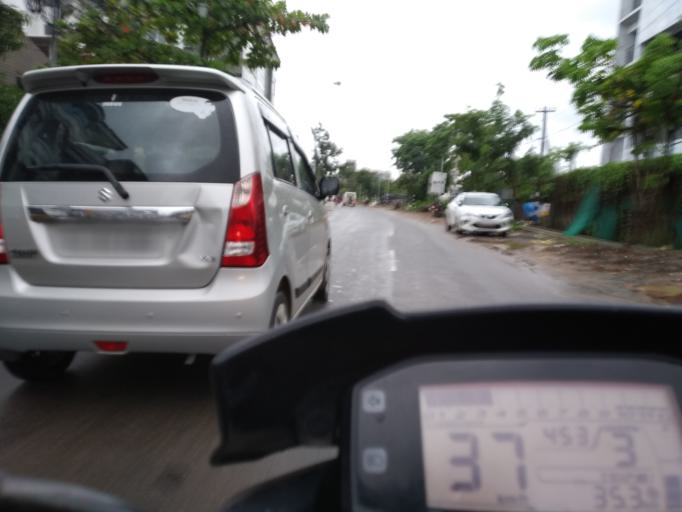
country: IN
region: Kerala
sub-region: Ernakulam
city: Cochin
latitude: 9.9728
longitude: 76.3070
